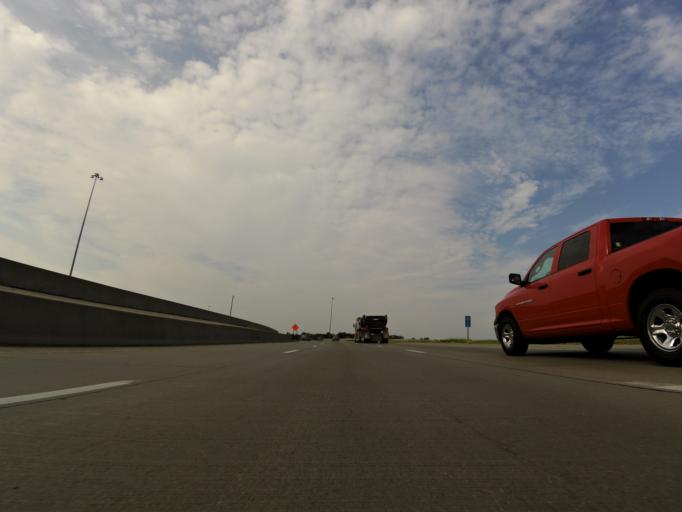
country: US
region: Kansas
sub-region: Sedgwick County
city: Wichita
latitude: 37.7213
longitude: -97.3186
